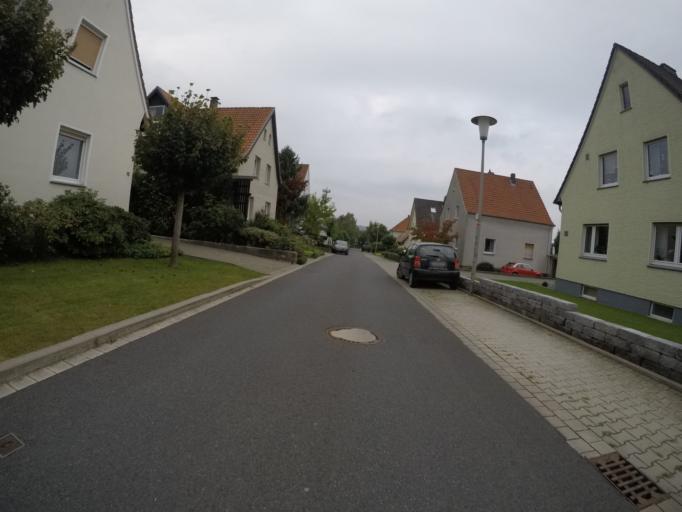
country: DE
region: North Rhine-Westphalia
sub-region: Regierungsbezirk Detmold
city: Herford
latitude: 52.1256
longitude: 8.6363
